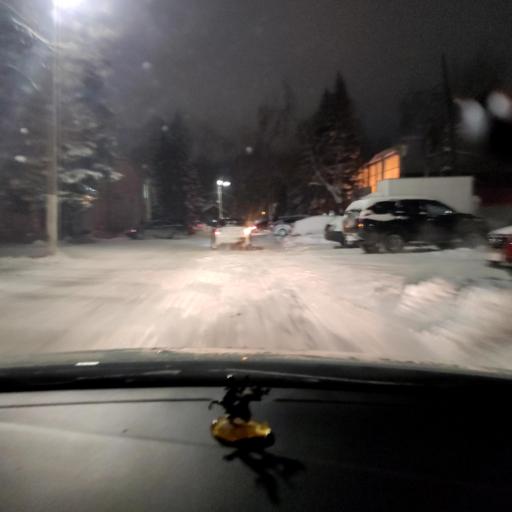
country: RU
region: Tatarstan
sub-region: Zelenodol'skiy Rayon
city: Zelenodolsk
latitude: 55.8458
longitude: 48.4968
